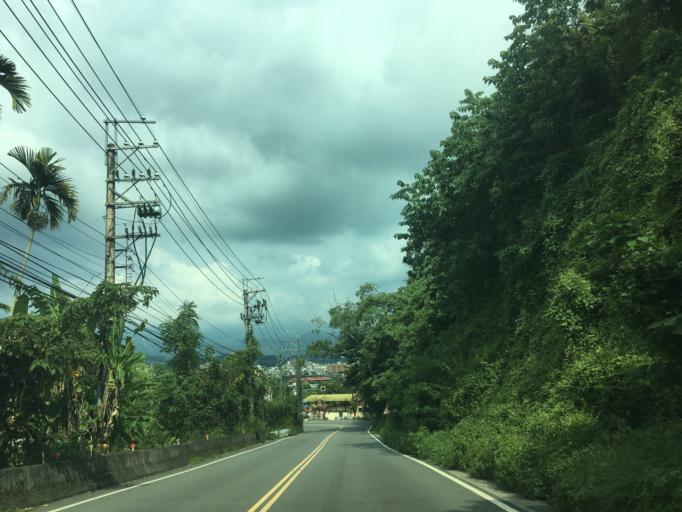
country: TW
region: Taiwan
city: Fengyuan
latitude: 24.2587
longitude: 120.8141
